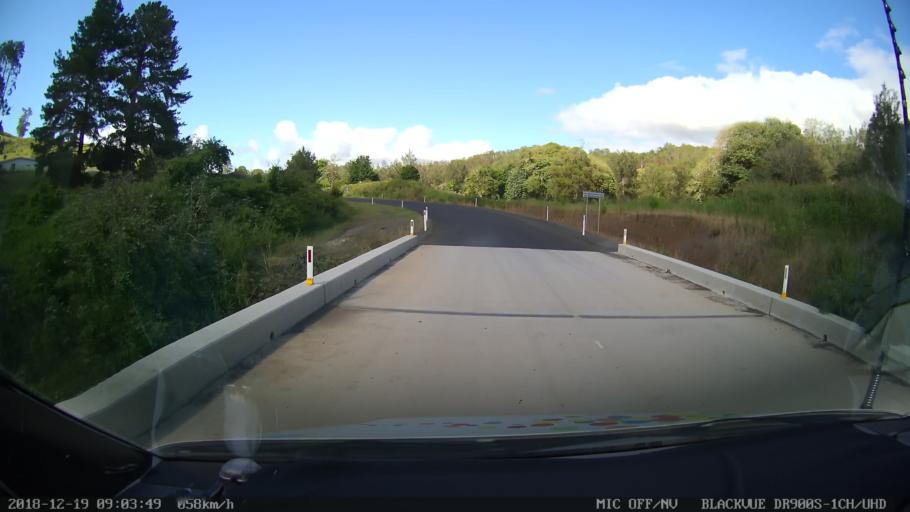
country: AU
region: New South Wales
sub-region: Kyogle
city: Kyogle
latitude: -28.4505
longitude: 152.9493
